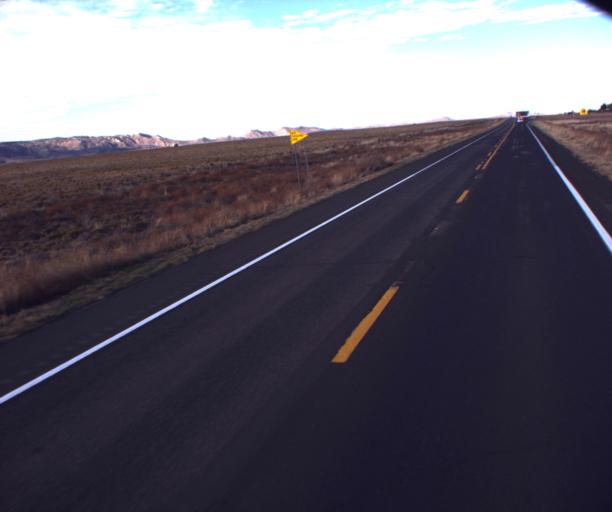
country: US
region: Arizona
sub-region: Apache County
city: Lukachukai
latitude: 36.9607
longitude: -109.3777
